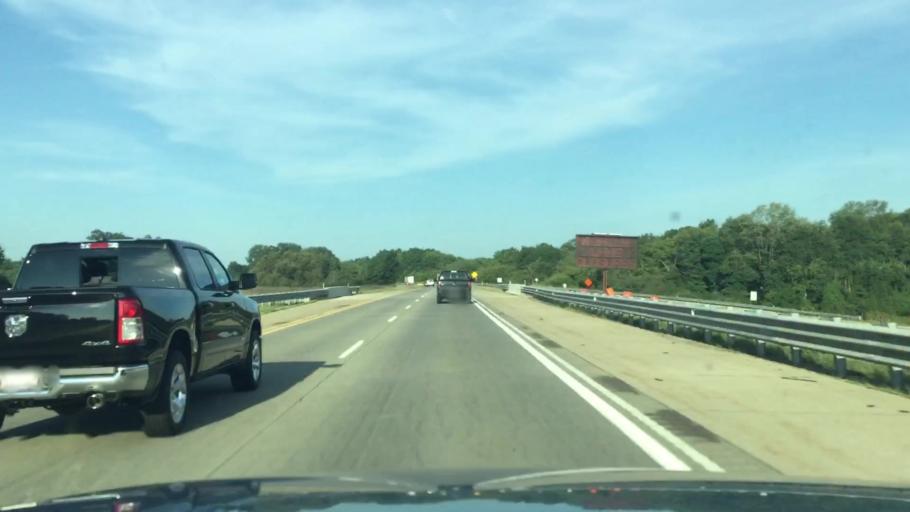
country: US
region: Michigan
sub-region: Jackson County
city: Grass Lake
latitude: 42.2920
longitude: -84.2590
